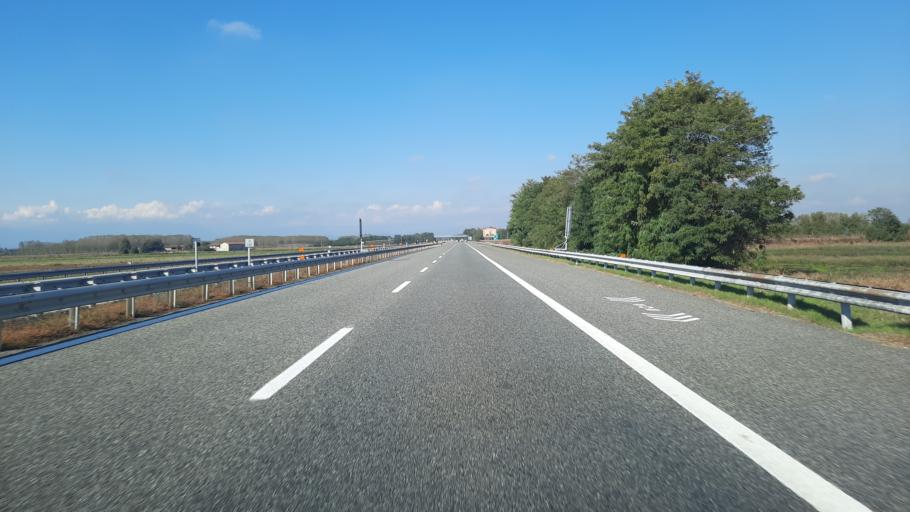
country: IT
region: Piedmont
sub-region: Provincia di Novara
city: Mandello Vitta
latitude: 45.4881
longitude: 8.4425
